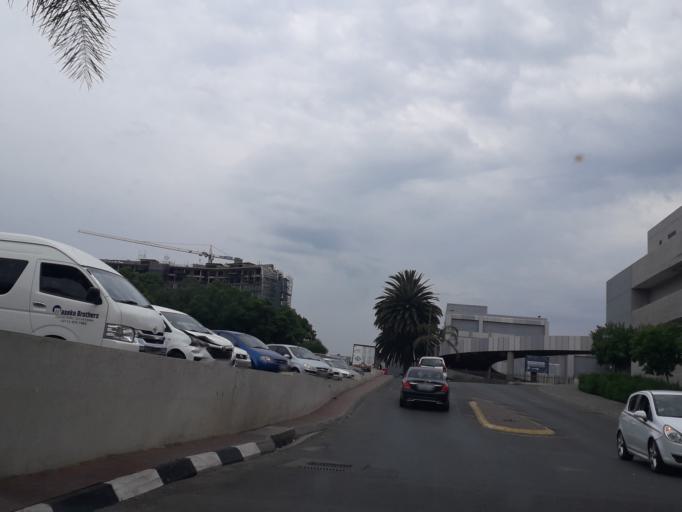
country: ZA
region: Gauteng
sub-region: City of Johannesburg Metropolitan Municipality
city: Johannesburg
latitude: -26.1779
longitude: 28.1181
